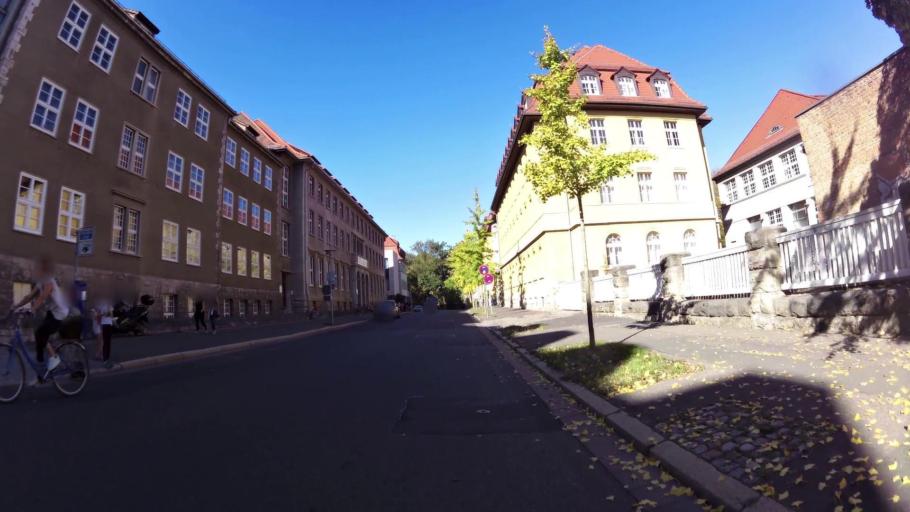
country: DE
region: Thuringia
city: Weimar
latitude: 50.9819
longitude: 11.3224
